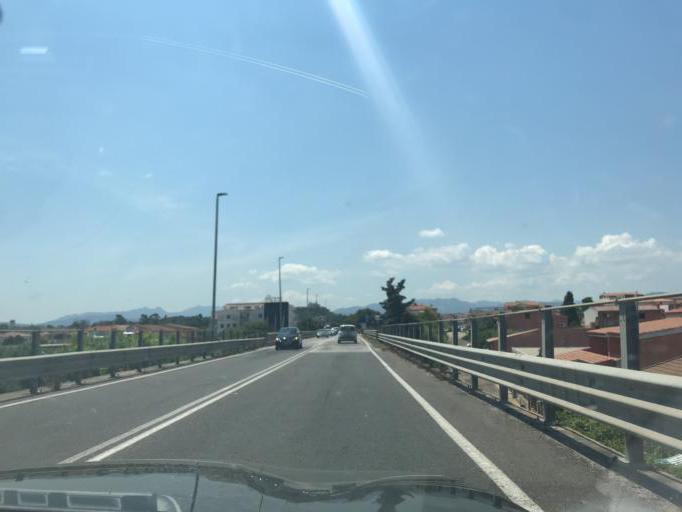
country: IT
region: Sardinia
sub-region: Provincia di Olbia-Tempio
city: Olbia
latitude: 40.9166
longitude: 9.5015
